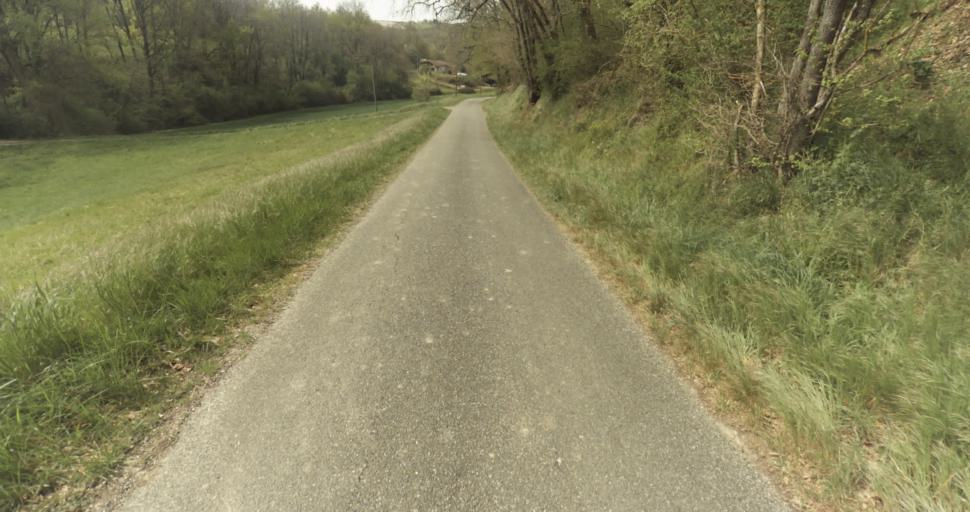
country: FR
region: Midi-Pyrenees
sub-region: Departement du Tarn-et-Garonne
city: Moissac
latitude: 44.1060
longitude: 1.0604
